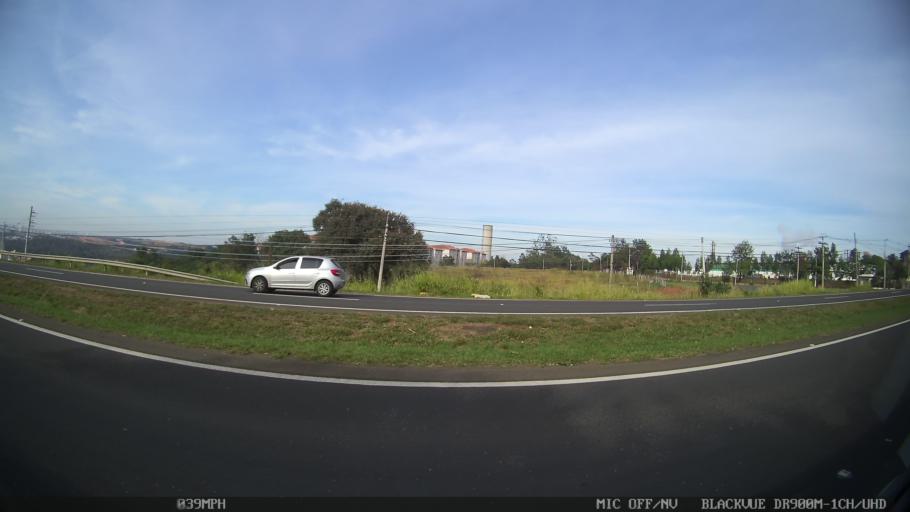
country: BR
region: Sao Paulo
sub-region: Piracicaba
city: Piracicaba
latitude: -22.6805
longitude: -47.6998
